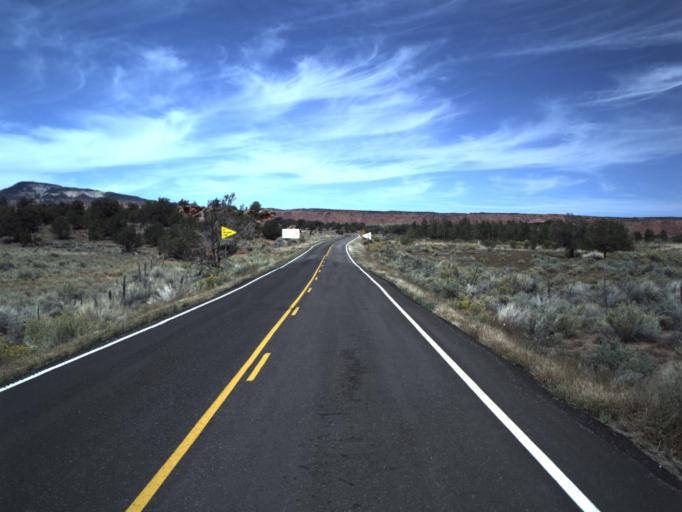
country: US
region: Utah
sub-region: Wayne County
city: Loa
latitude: 38.2860
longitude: -111.3956
